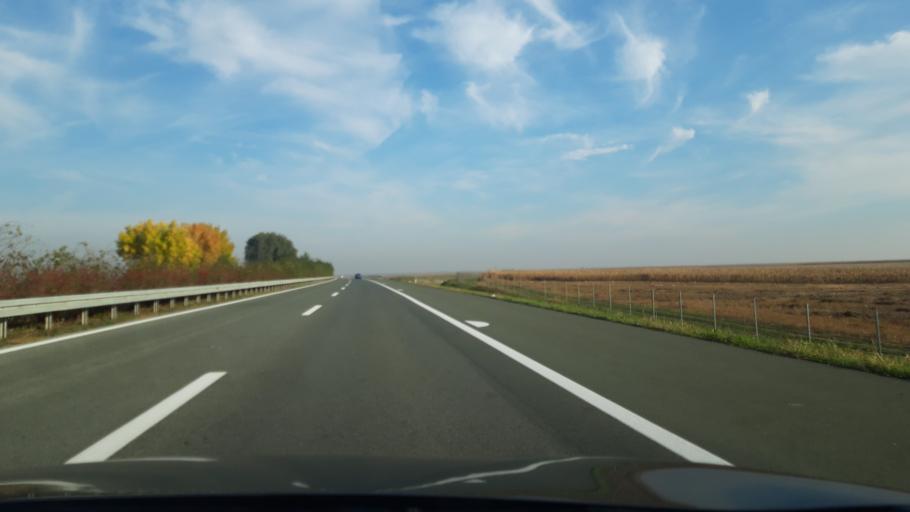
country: RS
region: Autonomna Pokrajina Vojvodina
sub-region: Severnobacki Okrug
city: Mali Igos
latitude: 45.6732
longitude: 19.7288
